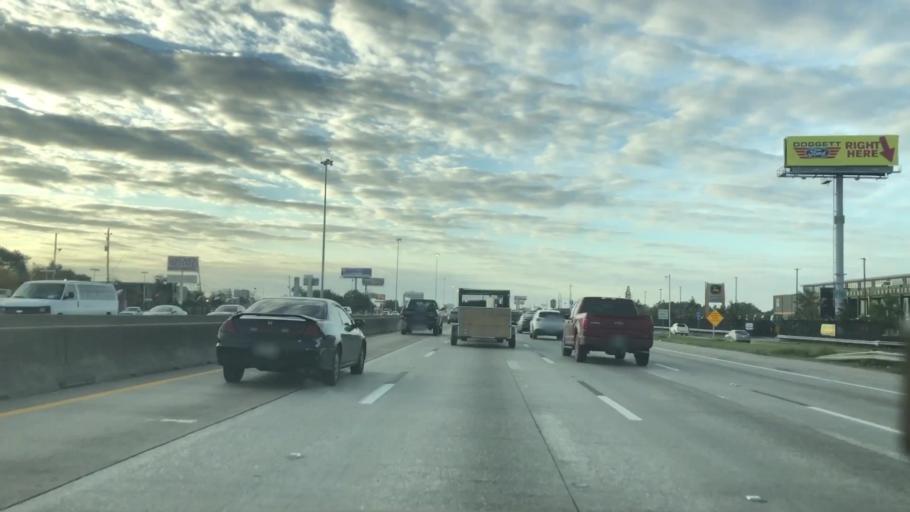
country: US
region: Texas
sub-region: Harris County
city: Aldine
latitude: 29.8944
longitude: -95.4123
